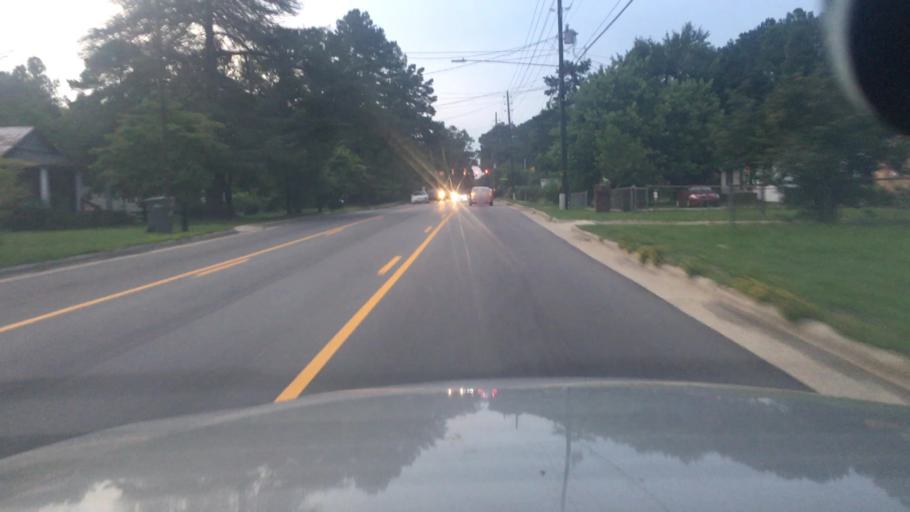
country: US
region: North Carolina
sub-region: Cumberland County
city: Hope Mills
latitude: 34.9641
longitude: -78.9434
